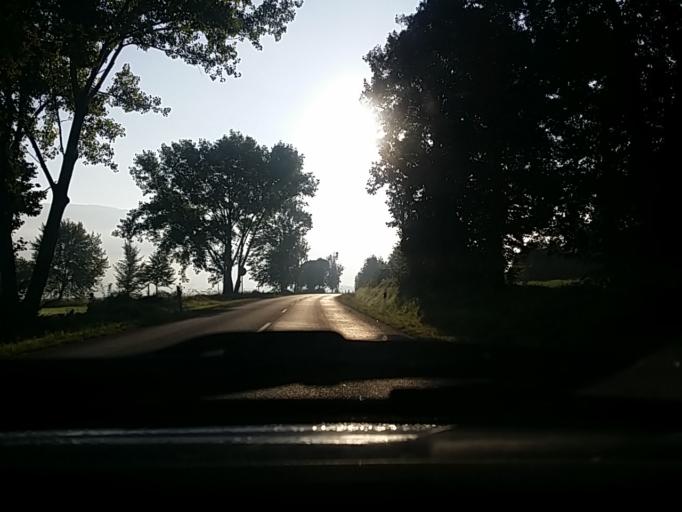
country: HU
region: Komarom-Esztergom
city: Pilismarot
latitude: 47.7793
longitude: 18.8877
